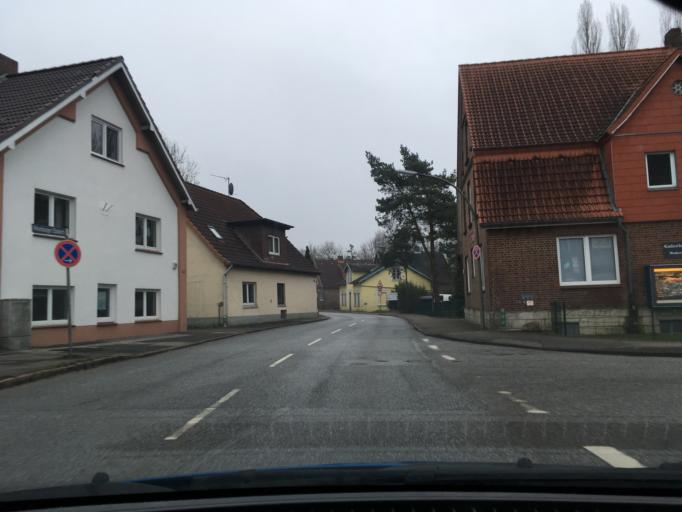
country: DE
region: Hamburg
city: Harburg
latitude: 53.4898
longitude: 9.9367
